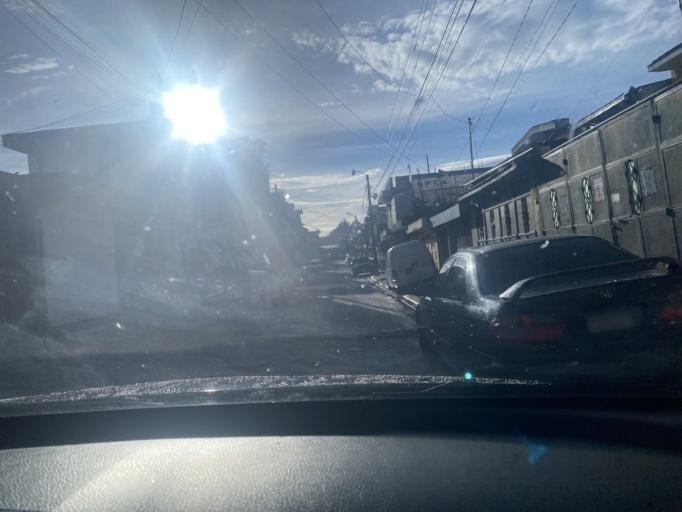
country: GT
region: Quetzaltenango
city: Olintepeque
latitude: 14.8639
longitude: -91.5201
